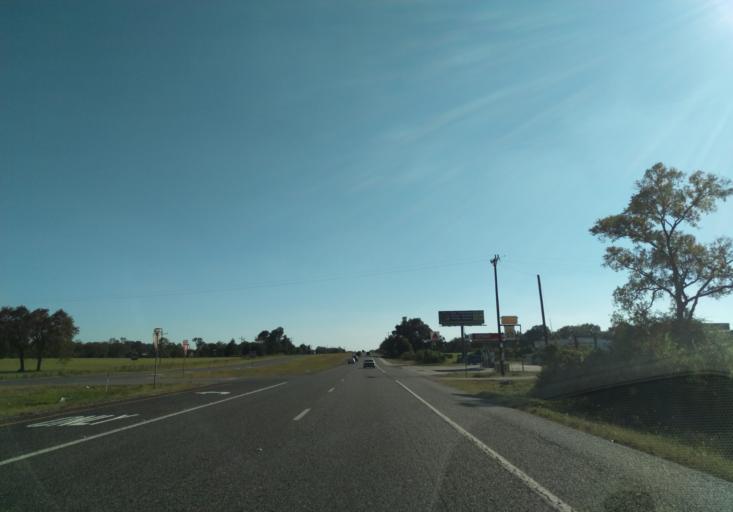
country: US
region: Texas
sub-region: Waller County
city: Hempstead
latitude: 30.2133
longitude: -96.0580
